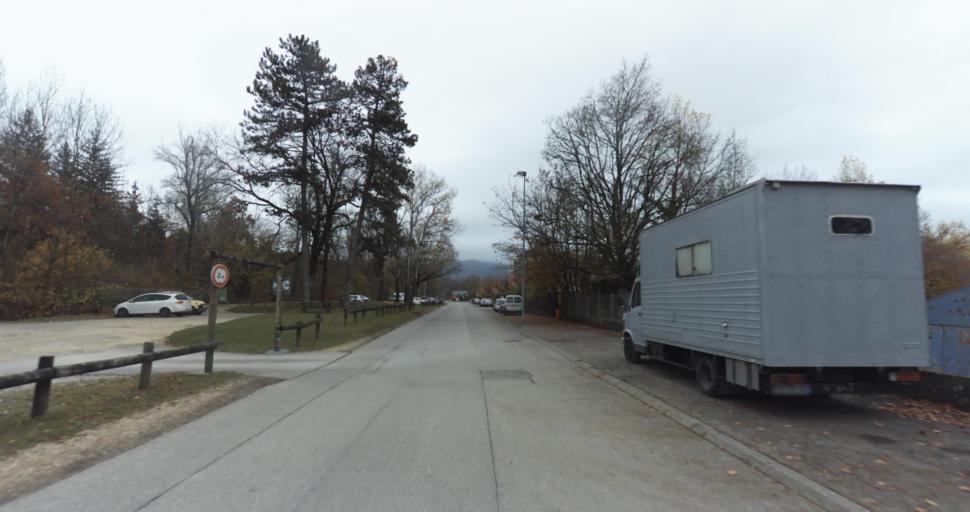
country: FR
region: Rhone-Alpes
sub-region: Departement de la Haute-Savoie
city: Meythet
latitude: 45.9188
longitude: 6.1047
